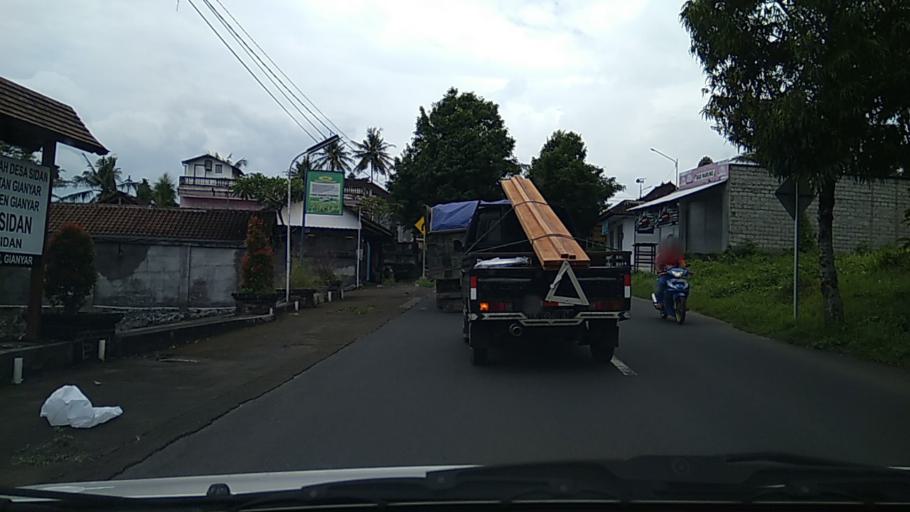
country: ID
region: Bali
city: Banjar Kelodan
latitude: -8.5355
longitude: 115.3485
